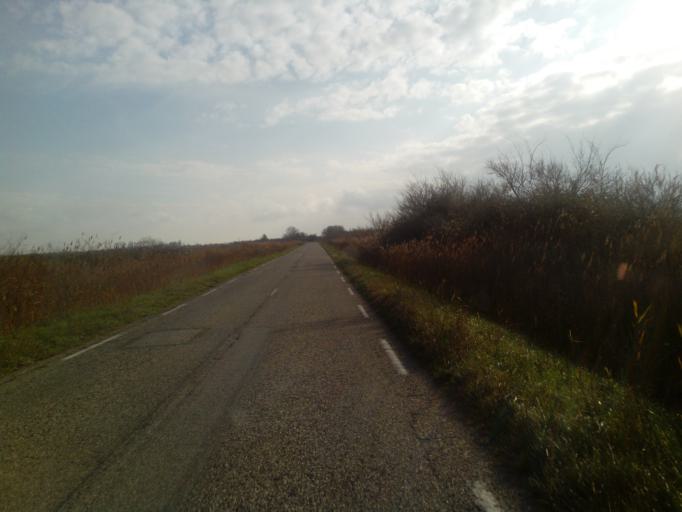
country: FR
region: Languedoc-Roussillon
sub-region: Departement du Gard
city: Saint-Gilles
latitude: 43.5973
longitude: 4.4900
